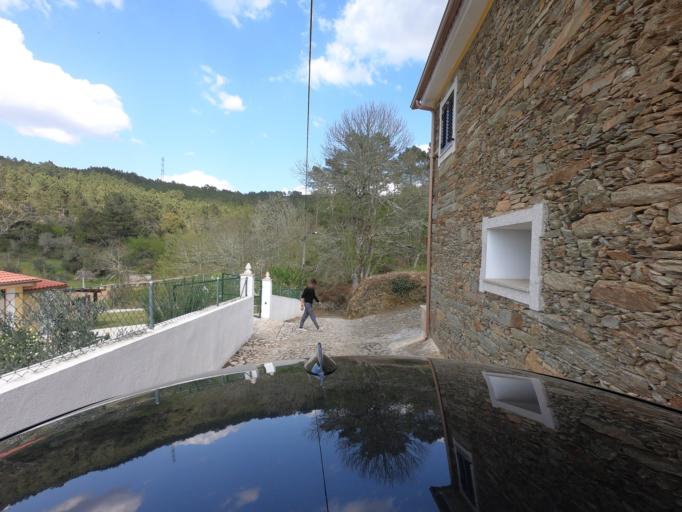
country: PT
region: Vila Real
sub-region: Sabrosa
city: Vilela
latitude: 41.2393
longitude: -7.6754
